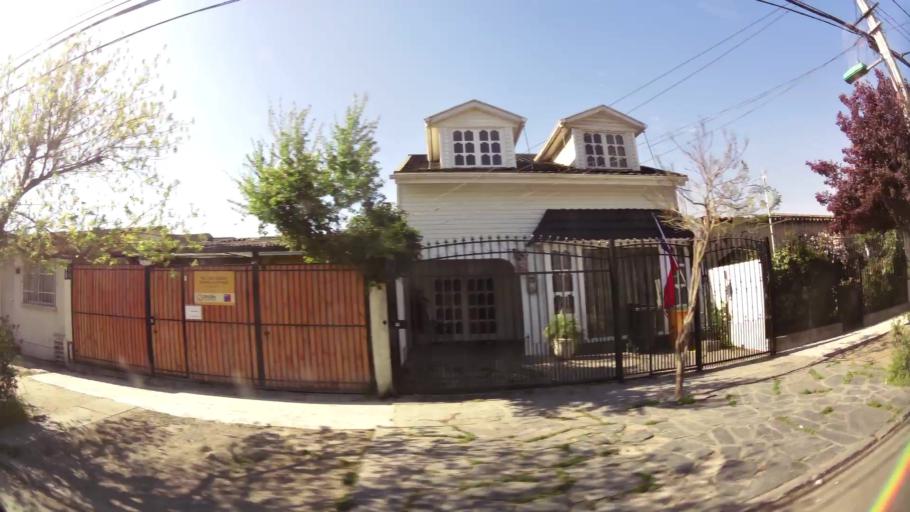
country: CL
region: Santiago Metropolitan
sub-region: Provincia de Santiago
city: Santiago
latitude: -33.5061
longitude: -70.6928
